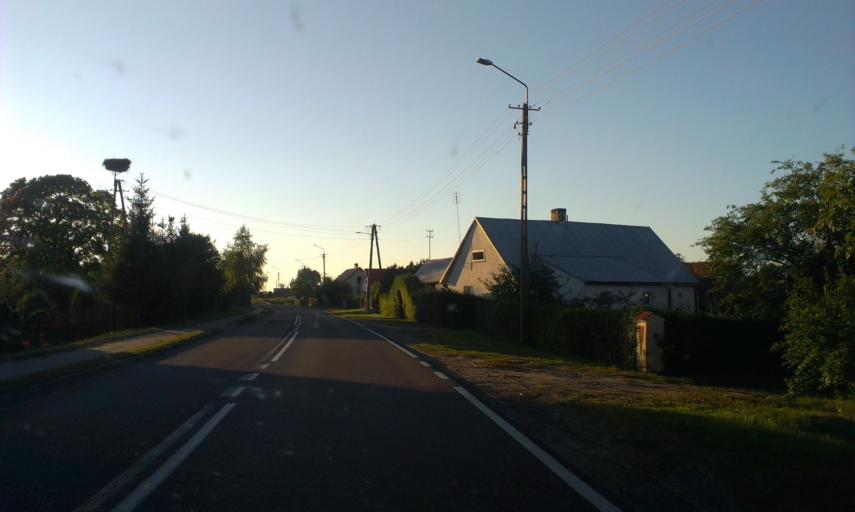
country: PL
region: West Pomeranian Voivodeship
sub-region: Powiat szczecinecki
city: Szczecinek
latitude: 53.7328
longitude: 16.8210
